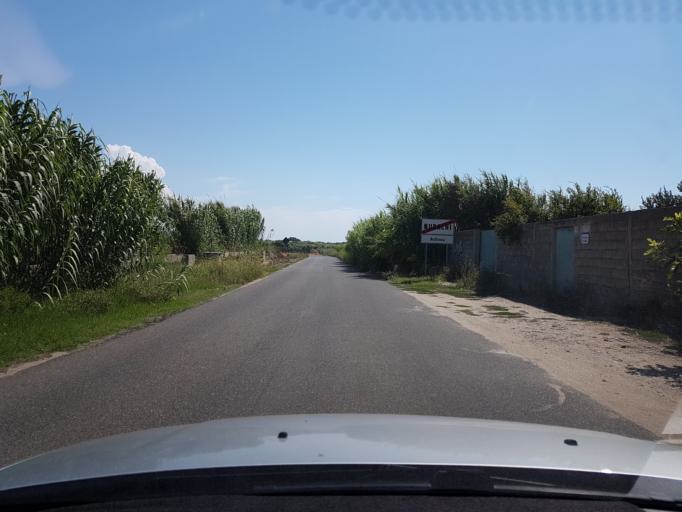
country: IT
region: Sardinia
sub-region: Provincia di Oristano
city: Nurachi
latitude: 39.9697
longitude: 8.5361
